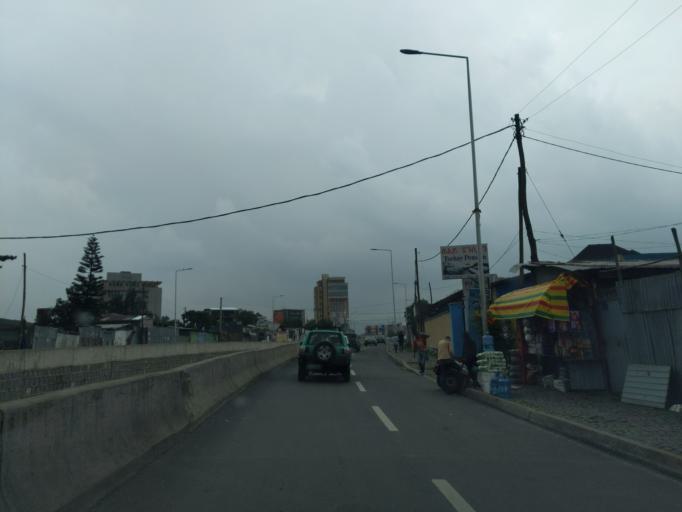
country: ET
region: Adis Abeba
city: Addis Ababa
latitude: 8.9846
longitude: 38.7655
